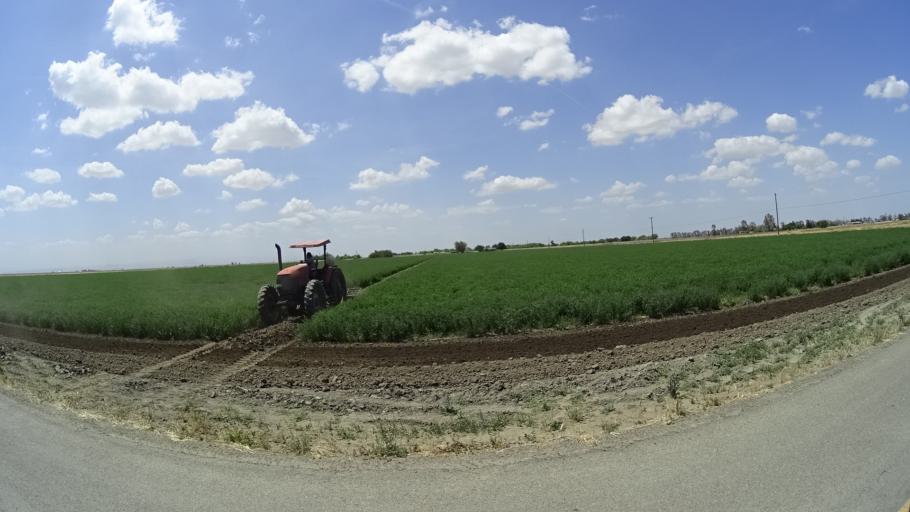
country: US
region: California
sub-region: Kings County
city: Stratford
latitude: 36.1812
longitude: -119.8253
